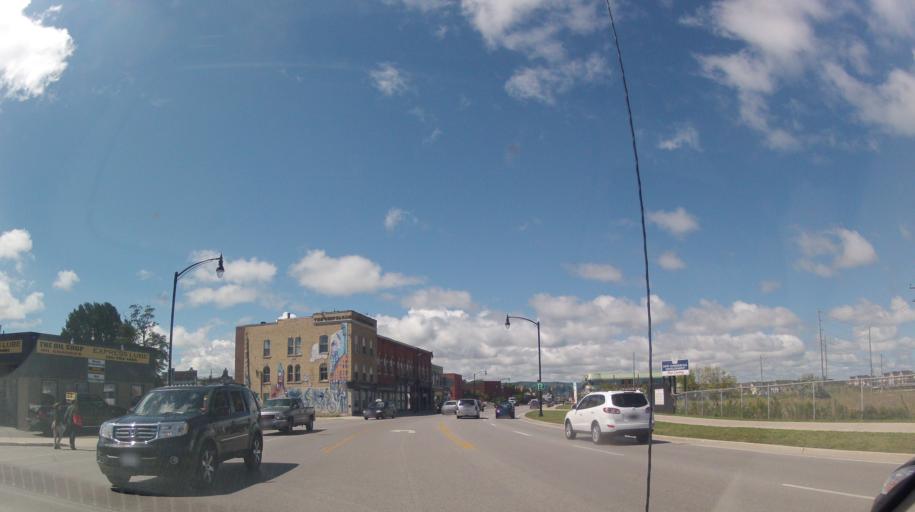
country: CA
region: Ontario
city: Collingwood
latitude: 44.5032
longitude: -80.2152
